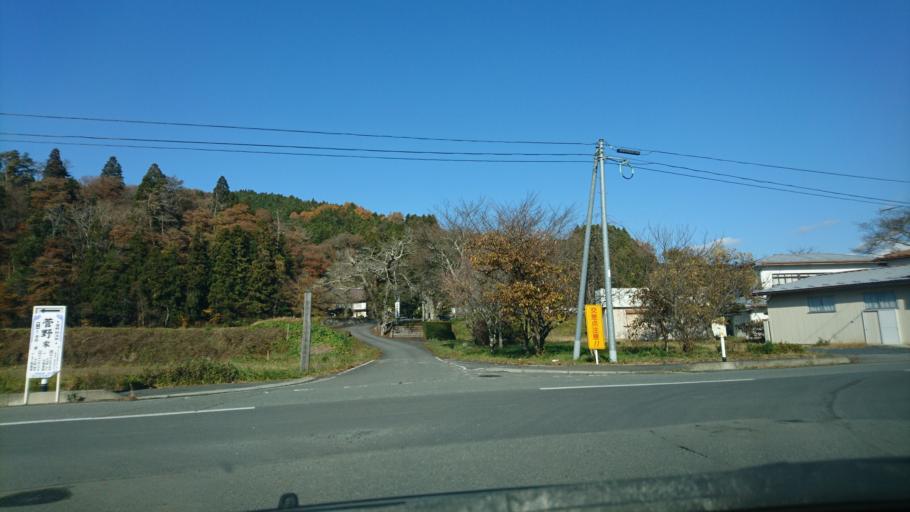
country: JP
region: Iwate
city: Ichinoseki
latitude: 39.0207
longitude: 141.4081
